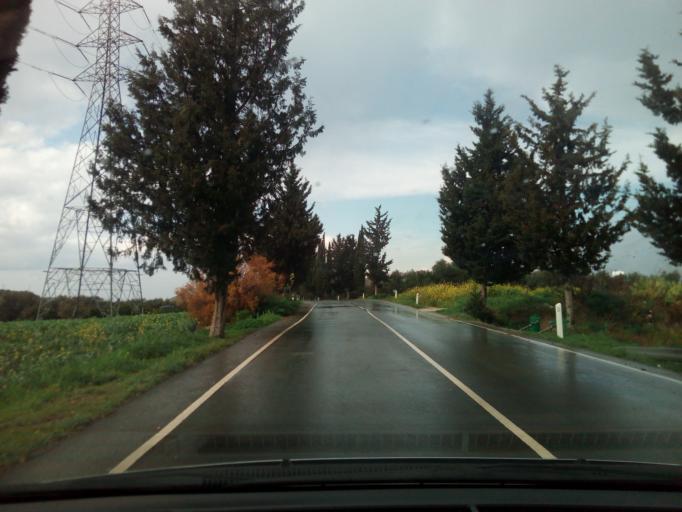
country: CY
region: Pafos
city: Polis
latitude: 35.0219
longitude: 32.4451
